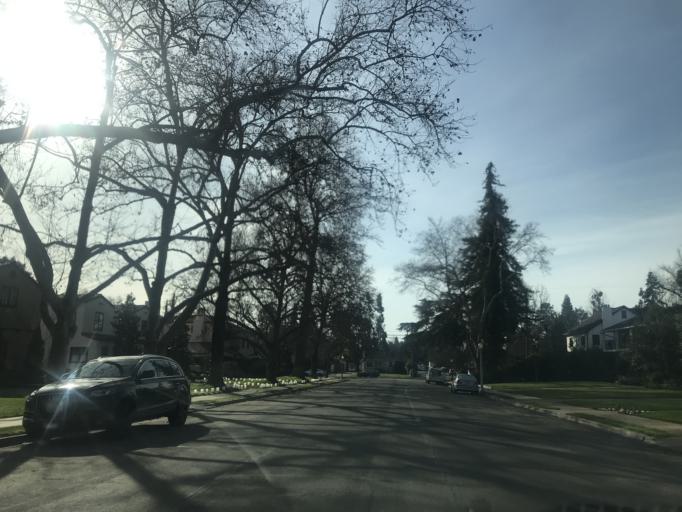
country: US
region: California
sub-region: Sacramento County
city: Sacramento
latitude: 38.5634
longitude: -121.4480
